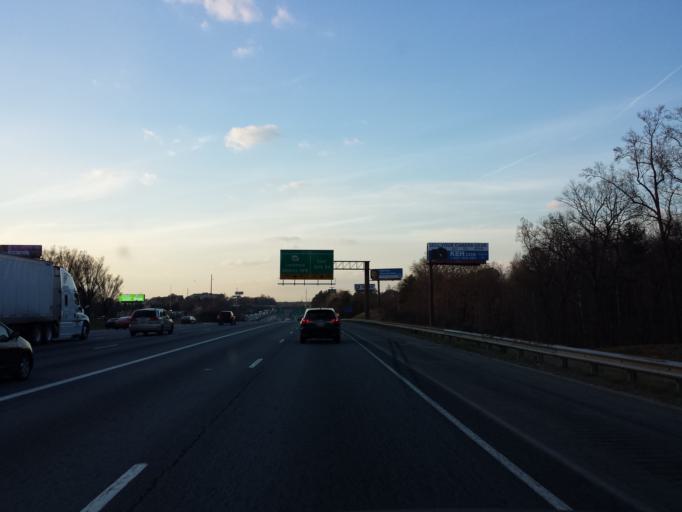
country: US
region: Georgia
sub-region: Cobb County
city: Smyrna
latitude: 33.9156
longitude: -84.4808
